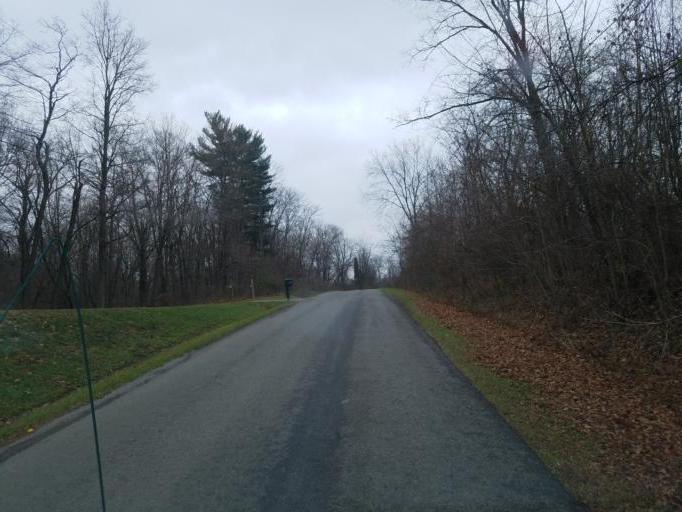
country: US
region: Ohio
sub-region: Morrow County
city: Cardington
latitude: 40.4180
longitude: -82.8512
